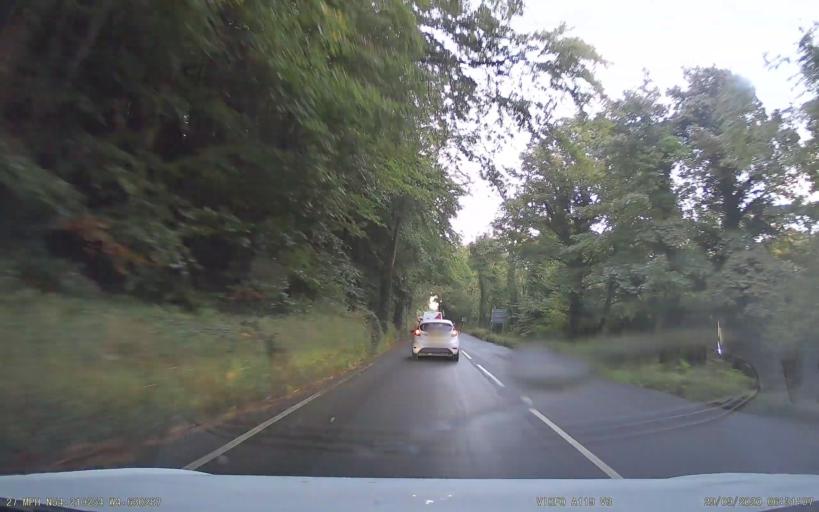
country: IM
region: Castletown
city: Castletown
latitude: 54.2103
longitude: -4.6303
